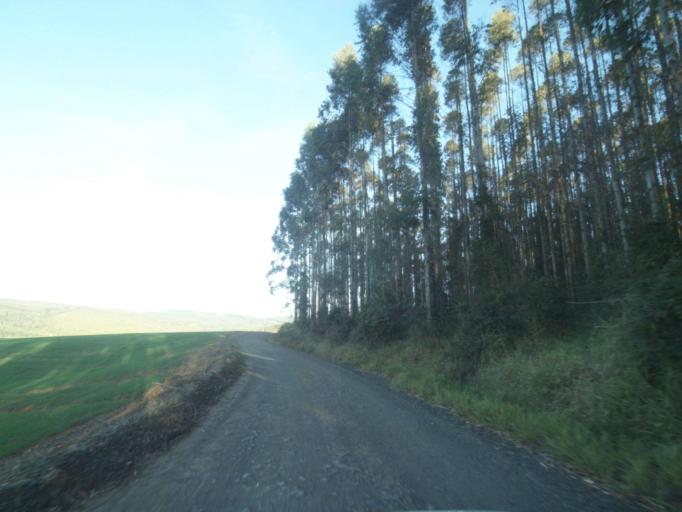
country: BR
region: Parana
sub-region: Telemaco Borba
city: Telemaco Borba
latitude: -24.4400
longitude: -50.6007
